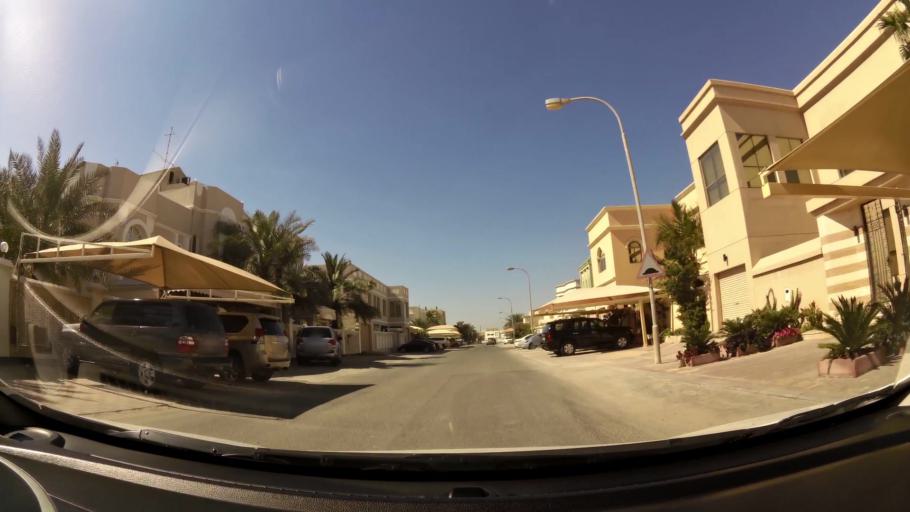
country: BH
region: Muharraq
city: Al Hadd
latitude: 26.2443
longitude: 50.6334
